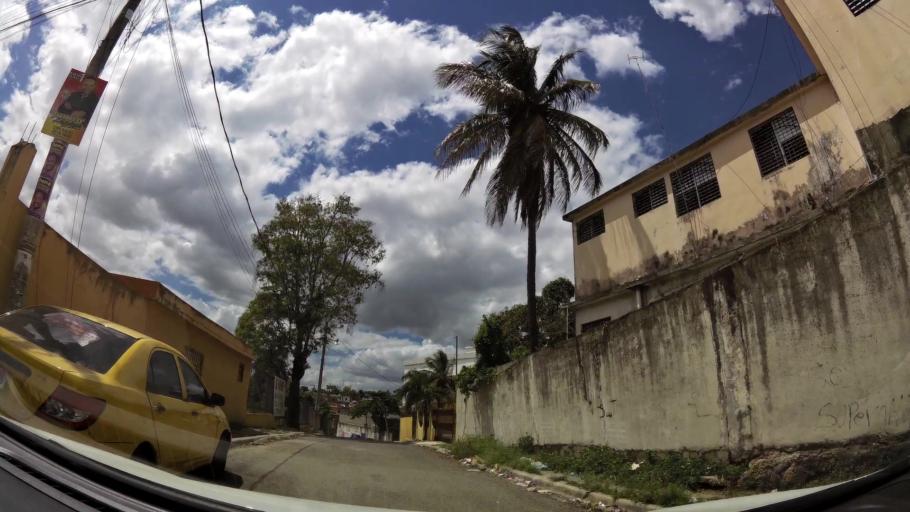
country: DO
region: Nacional
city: Ensanche Luperon
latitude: 18.5246
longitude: -69.9141
